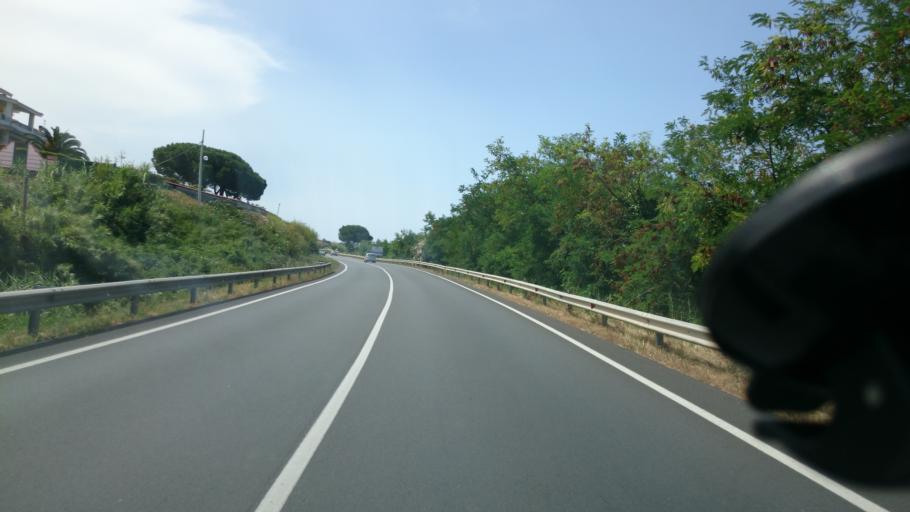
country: IT
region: Calabria
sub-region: Provincia di Cosenza
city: Diamante
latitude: 39.7002
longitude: 15.8140
